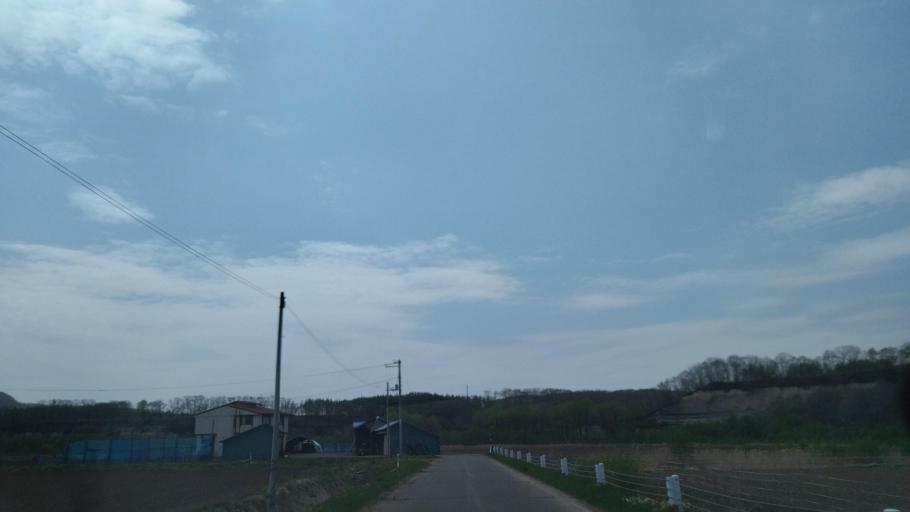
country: JP
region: Hokkaido
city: Otofuke
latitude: 43.3166
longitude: 143.5738
